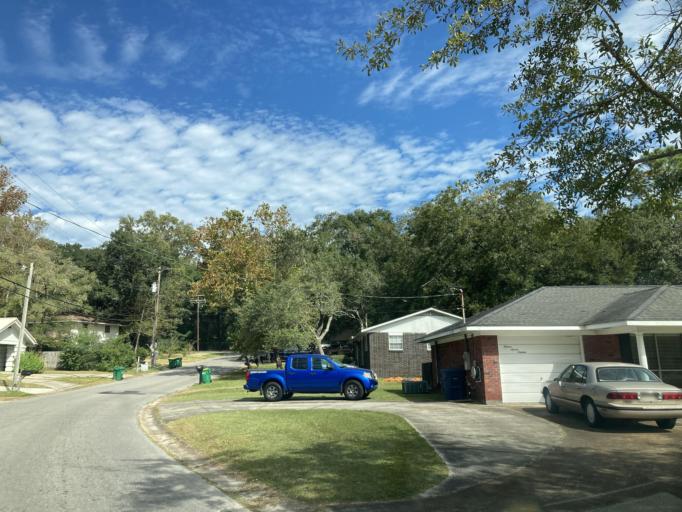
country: US
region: Mississippi
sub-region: Jackson County
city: Saint Martin
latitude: 30.4474
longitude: -88.8728
